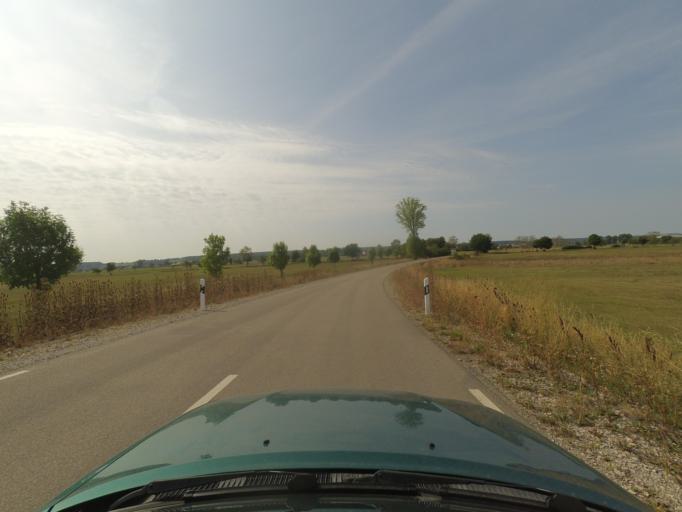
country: DE
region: Bavaria
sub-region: Regierungsbezirk Mittelfranken
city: Herrieden
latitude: 49.2313
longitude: 10.5210
